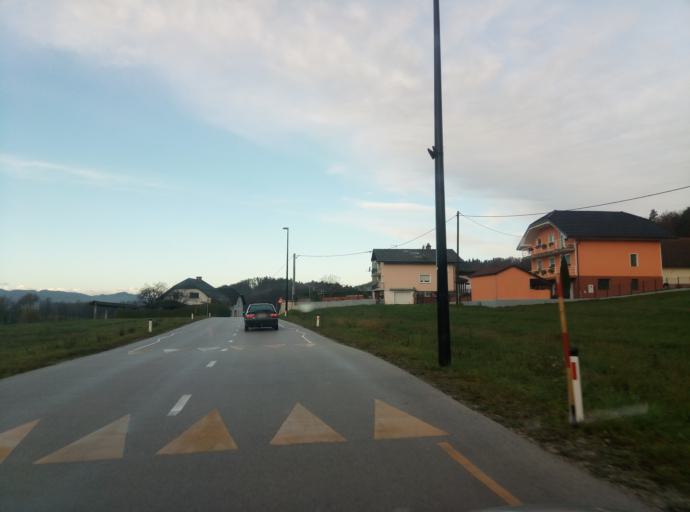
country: SI
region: Komenda
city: Moste
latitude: 46.1683
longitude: 14.5371
